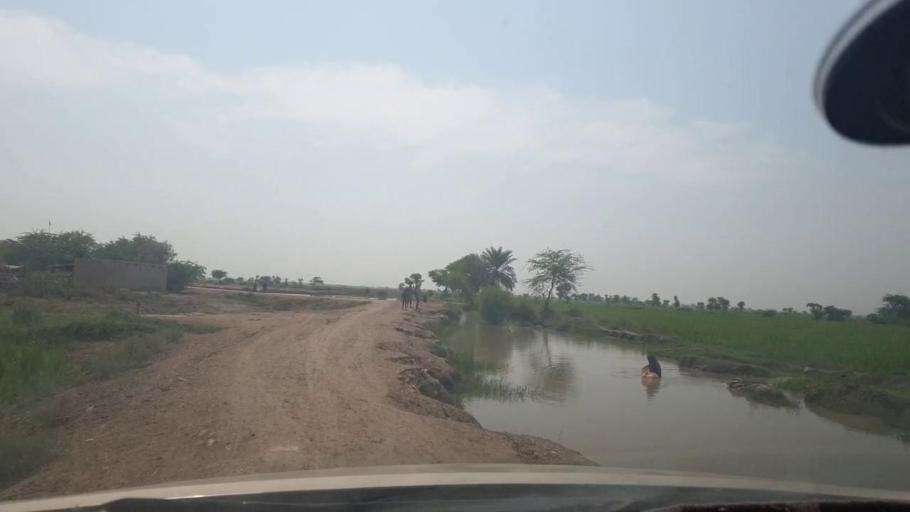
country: PK
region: Sindh
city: Jacobabad
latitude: 28.2741
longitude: 68.5256
